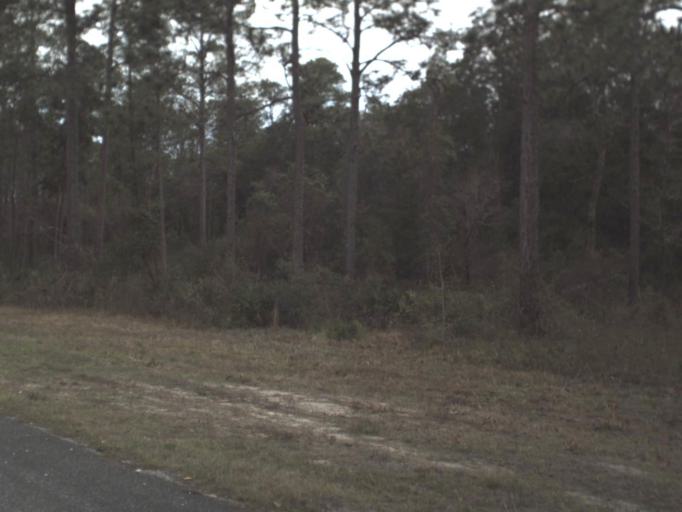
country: US
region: Florida
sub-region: Wakulla County
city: Crawfordville
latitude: 30.2947
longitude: -84.4106
